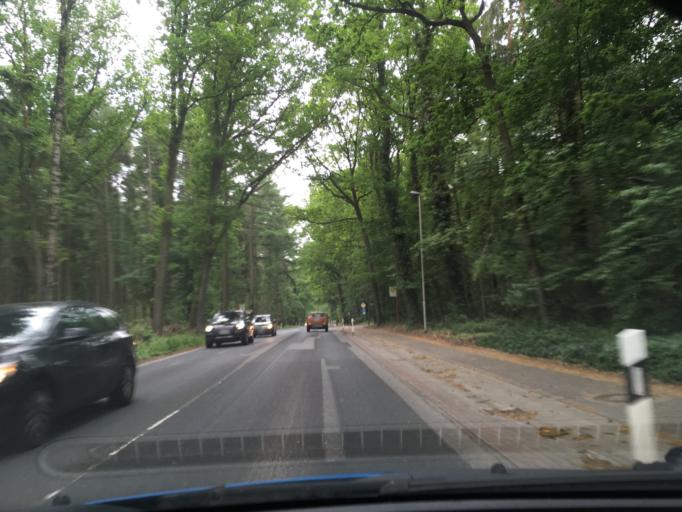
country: DE
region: Lower Saxony
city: Buchholz in der Nordheide
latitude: 53.3424
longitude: 9.8810
